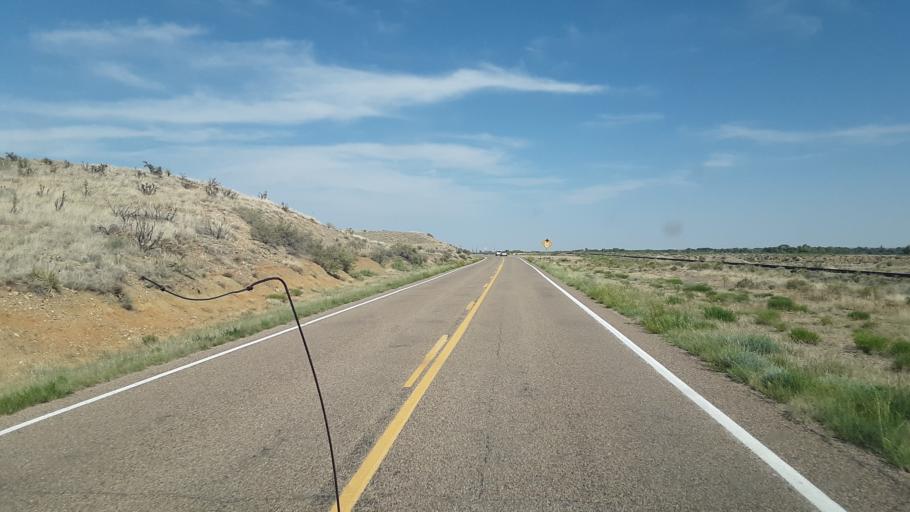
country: US
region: Colorado
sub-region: Otero County
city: Fowler
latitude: 38.1780
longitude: -104.1096
